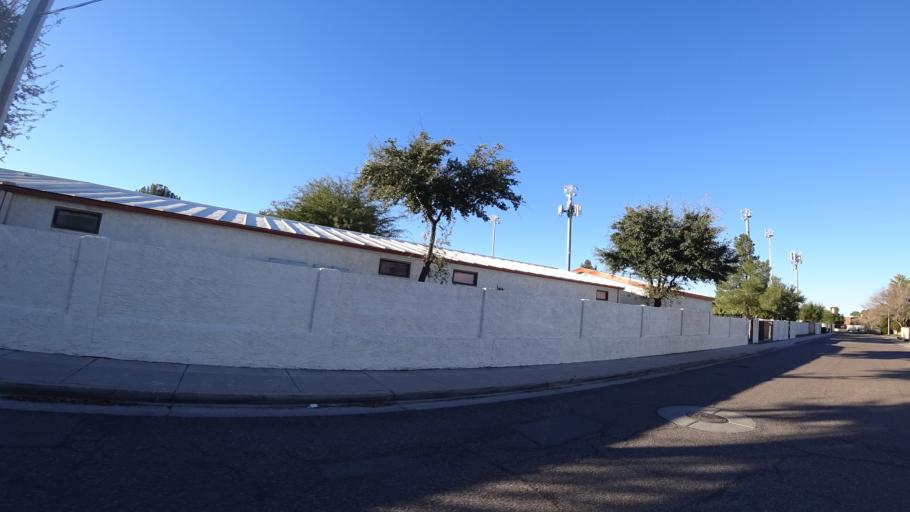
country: US
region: Arizona
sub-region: Maricopa County
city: Paradise Valley
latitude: 33.5063
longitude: -112.0093
